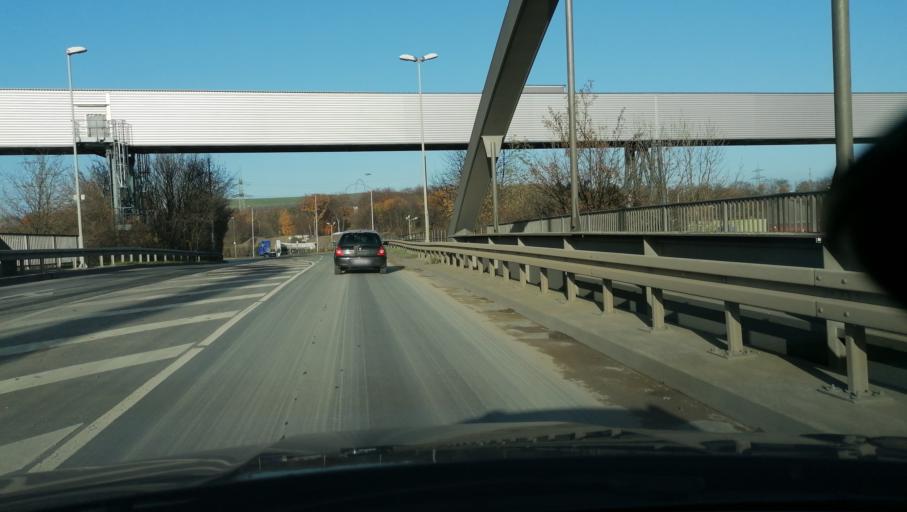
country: DE
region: North Rhine-Westphalia
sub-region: Regierungsbezirk Arnsberg
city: Herne
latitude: 51.5499
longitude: 7.1788
